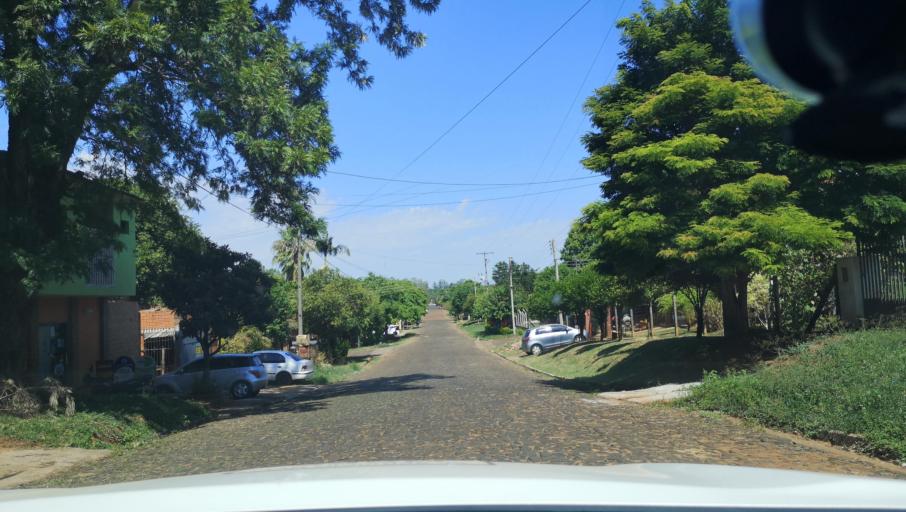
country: PY
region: Itapua
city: Carmen del Parana
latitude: -27.1577
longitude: -56.2338
